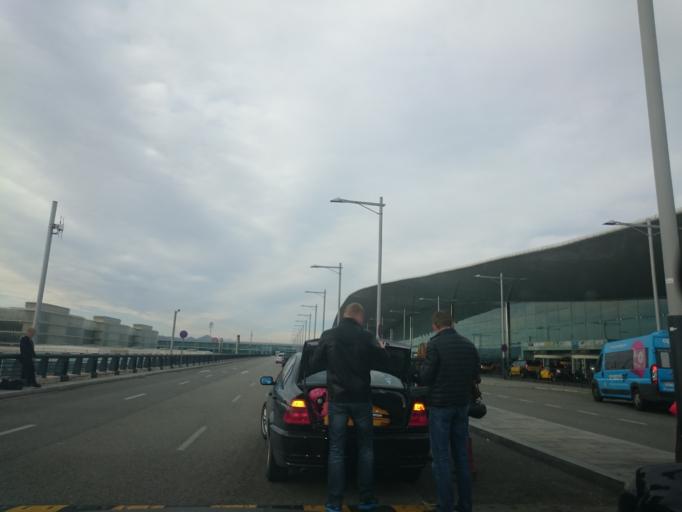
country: ES
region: Catalonia
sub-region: Provincia de Barcelona
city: El Prat de Llobregat
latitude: 41.2875
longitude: 2.0737
